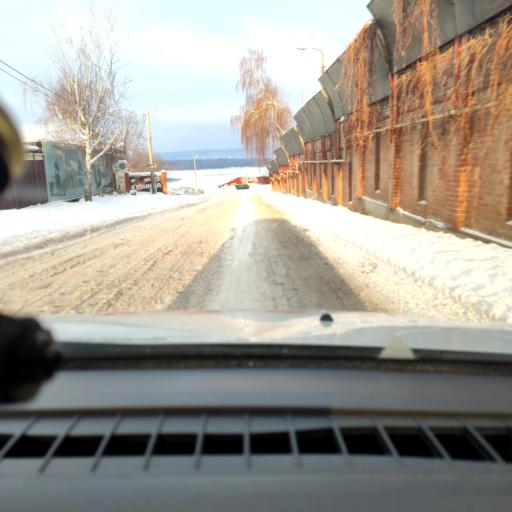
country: RU
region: Samara
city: Samara
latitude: 53.2771
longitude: 50.1893
